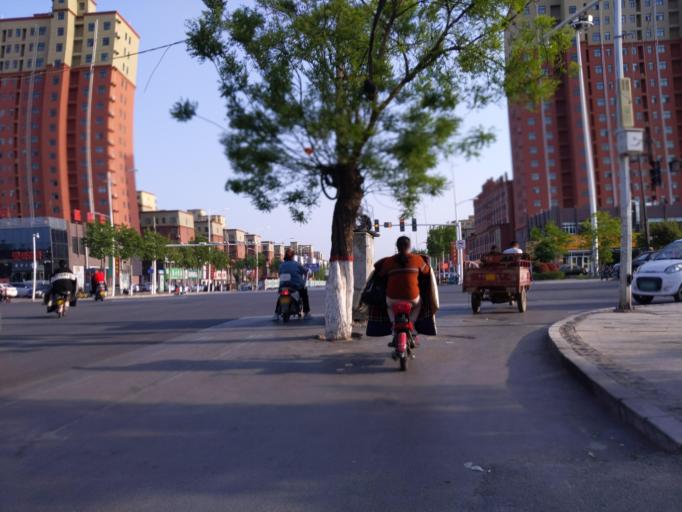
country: CN
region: Henan Sheng
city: Puyang Chengguanzhen
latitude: 35.6986
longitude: 115.0160
